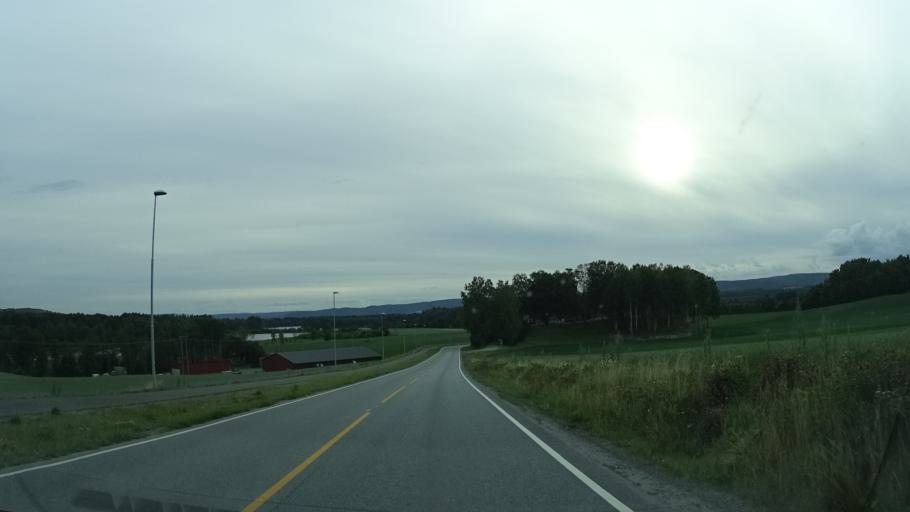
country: NO
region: Buskerud
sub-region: Ringerike
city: Honefoss
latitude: 60.1294
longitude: 10.2651
